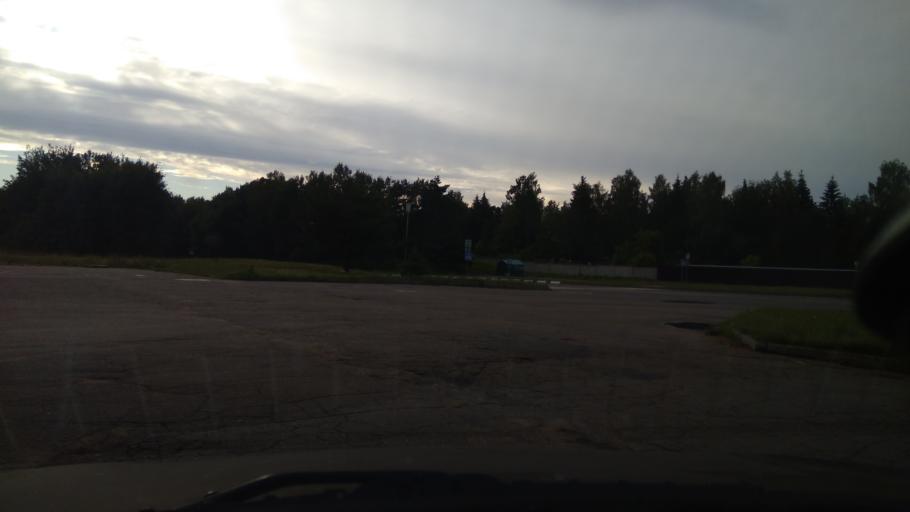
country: BY
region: Minsk
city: Bal'shavik
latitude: 53.9829
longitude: 27.5562
